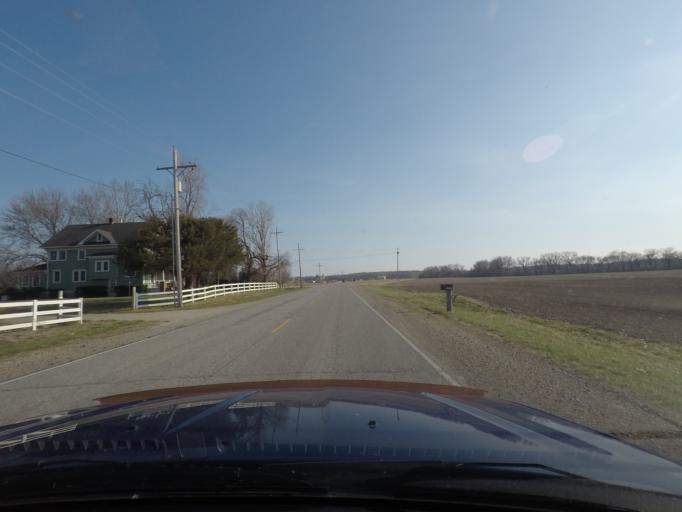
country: US
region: Kansas
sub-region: Jefferson County
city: Oskaloosa
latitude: 39.0634
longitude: -95.3819
